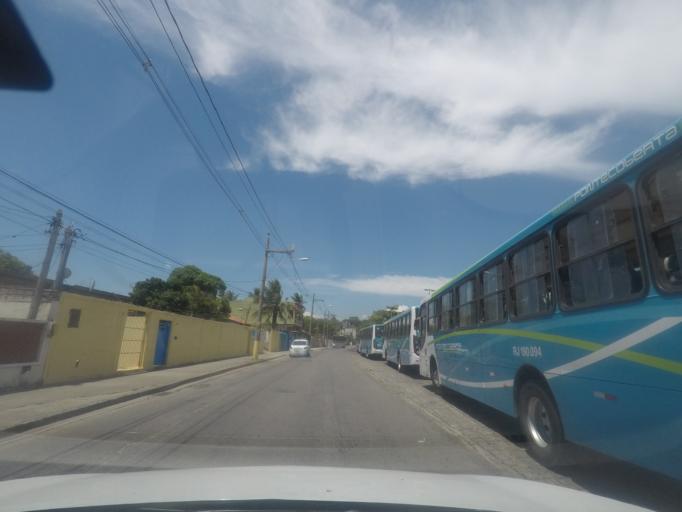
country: BR
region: Rio de Janeiro
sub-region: Itaguai
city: Itaguai
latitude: -22.9856
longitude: -43.6872
